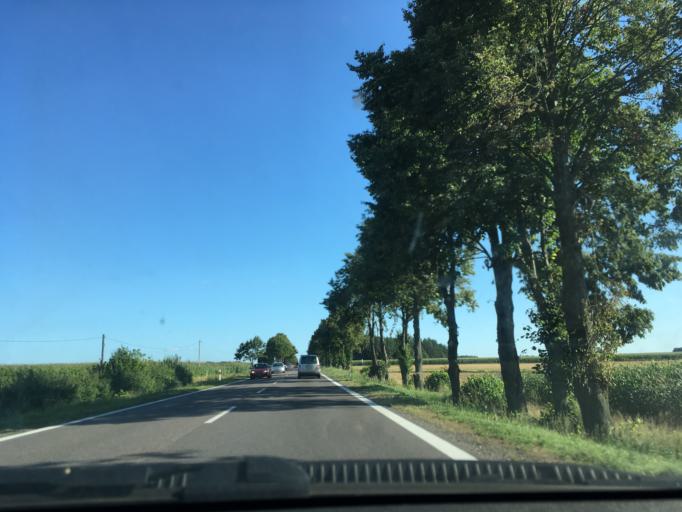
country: PL
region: Podlasie
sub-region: Powiat sokolski
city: Janow
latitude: 53.4335
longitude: 23.1007
